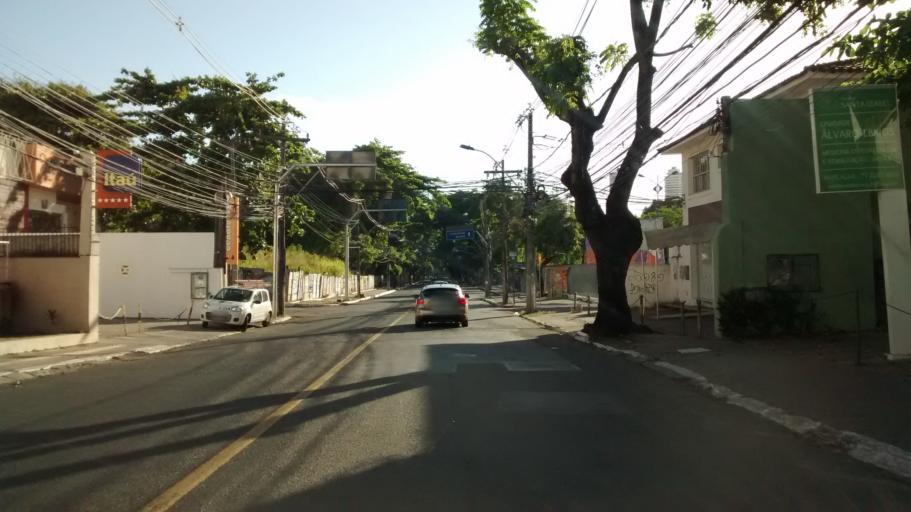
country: BR
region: Bahia
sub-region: Salvador
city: Salvador
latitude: -13.0018
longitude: -38.5059
